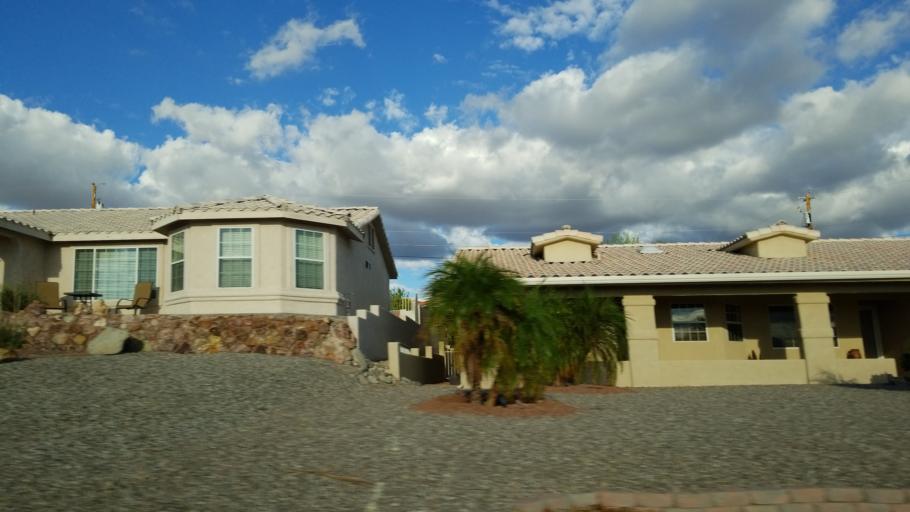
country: US
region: Arizona
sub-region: Mohave County
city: Lake Havasu City
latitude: 34.4614
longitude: -114.2592
